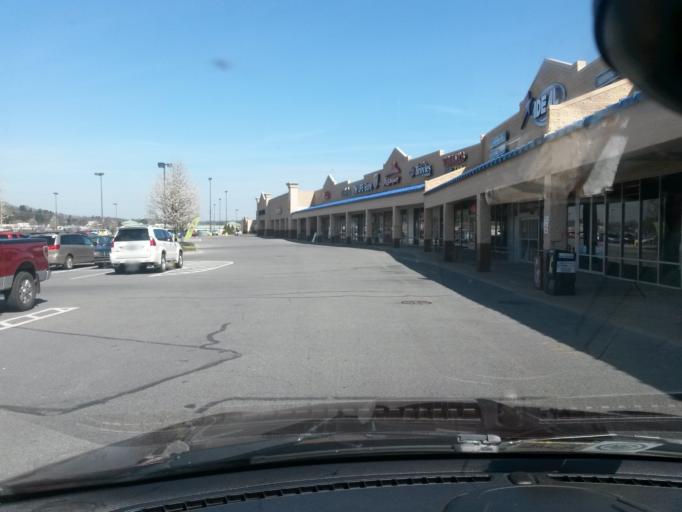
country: US
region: West Virginia
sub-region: Raleigh County
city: Beckley
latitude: 37.7995
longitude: -81.1758
